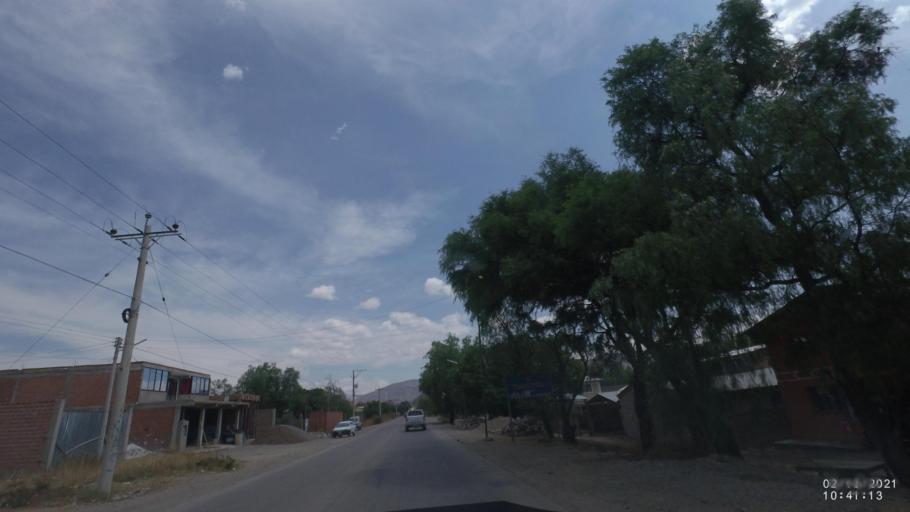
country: BO
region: Cochabamba
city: Capinota
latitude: -17.6156
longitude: -66.2900
